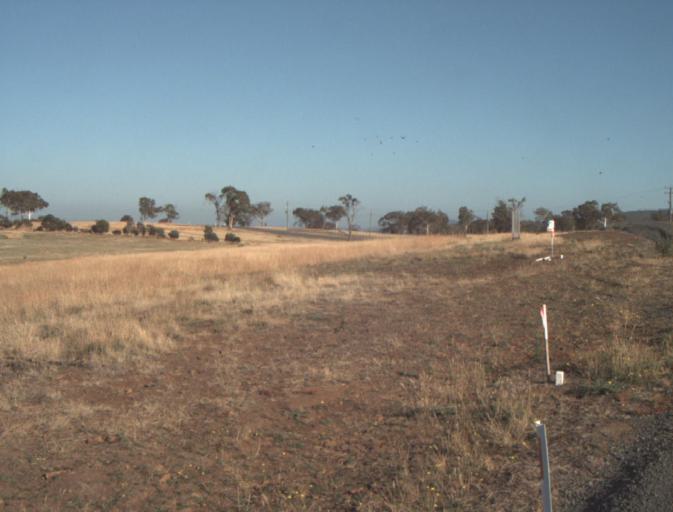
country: AU
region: Tasmania
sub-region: Launceston
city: Newstead
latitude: -41.4387
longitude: 147.2315
